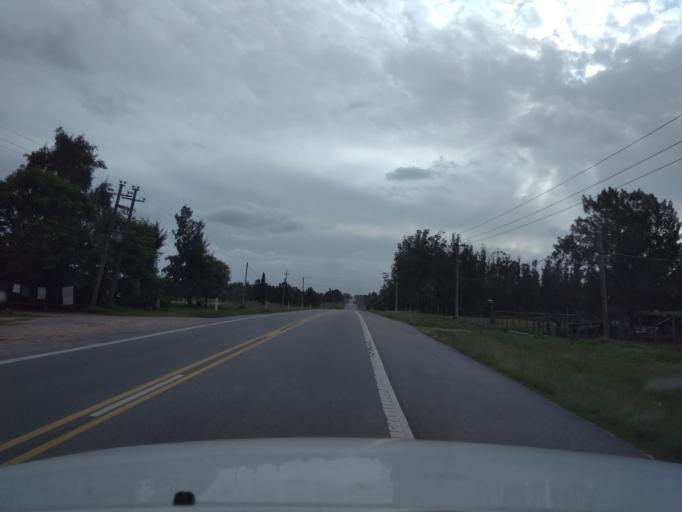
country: UY
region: Canelones
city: Joaquin Suarez
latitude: -34.7029
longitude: -56.0428
